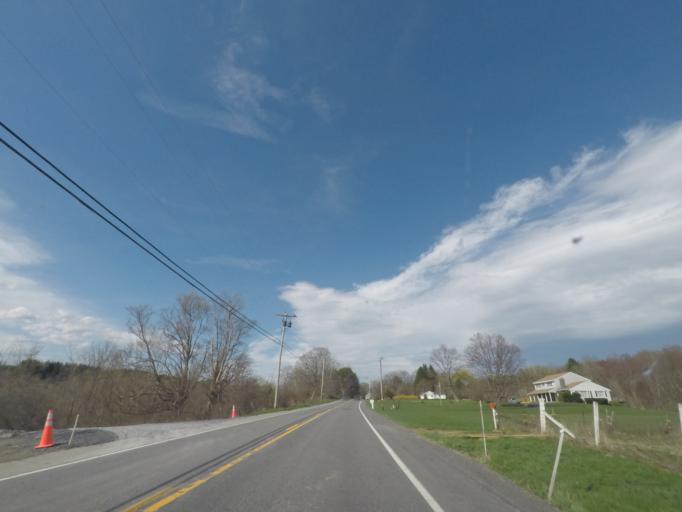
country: US
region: New York
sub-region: Greene County
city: Cairo
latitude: 42.4458
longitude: -74.0150
